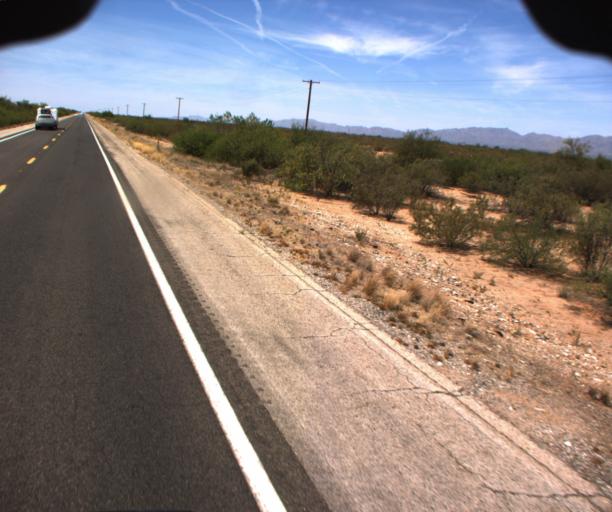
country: US
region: Arizona
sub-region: La Paz County
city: Salome
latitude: 33.9316
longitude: -113.2156
